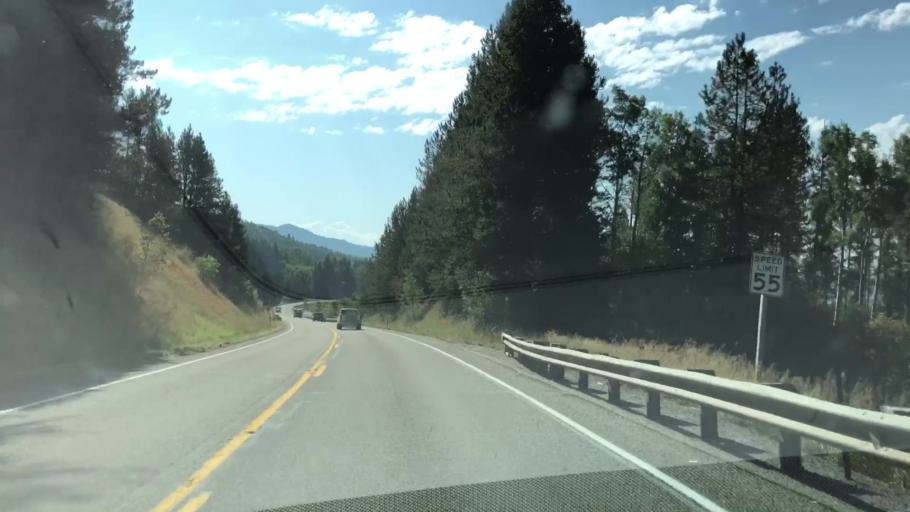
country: US
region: Idaho
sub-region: Teton County
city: Victor
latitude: 43.3037
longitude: -111.1338
